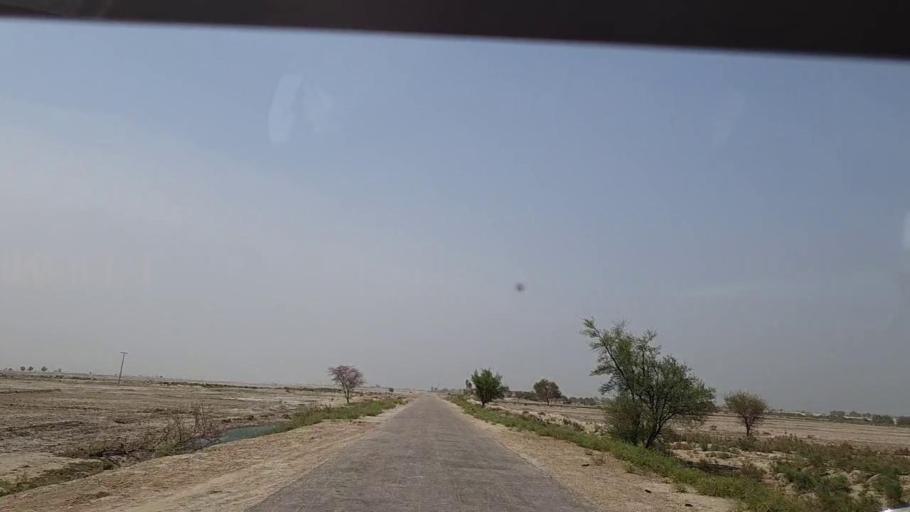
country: PK
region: Sindh
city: Khairpur Nathan Shah
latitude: 27.0590
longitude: 67.6480
